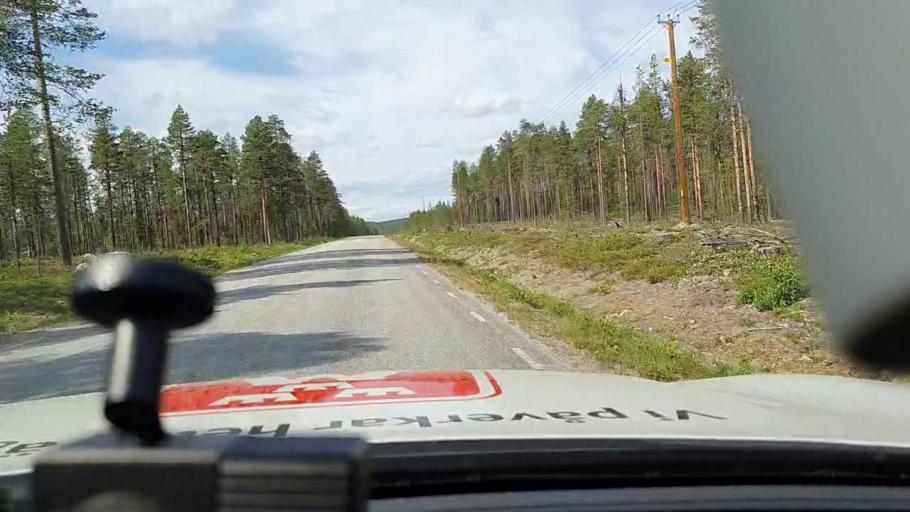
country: SE
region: Norrbotten
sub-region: Jokkmokks Kommun
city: Jokkmokk
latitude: 66.6233
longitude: 19.6840
